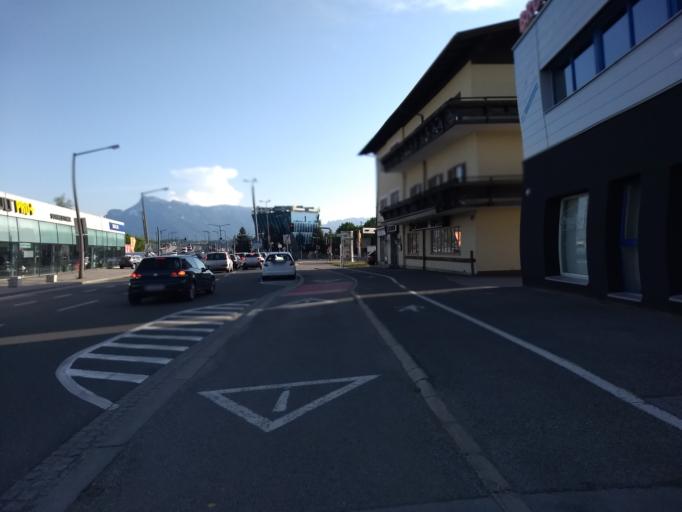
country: AT
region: Salzburg
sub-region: Politischer Bezirk Salzburg-Umgebung
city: Bergheim
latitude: 47.8262
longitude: 13.0553
